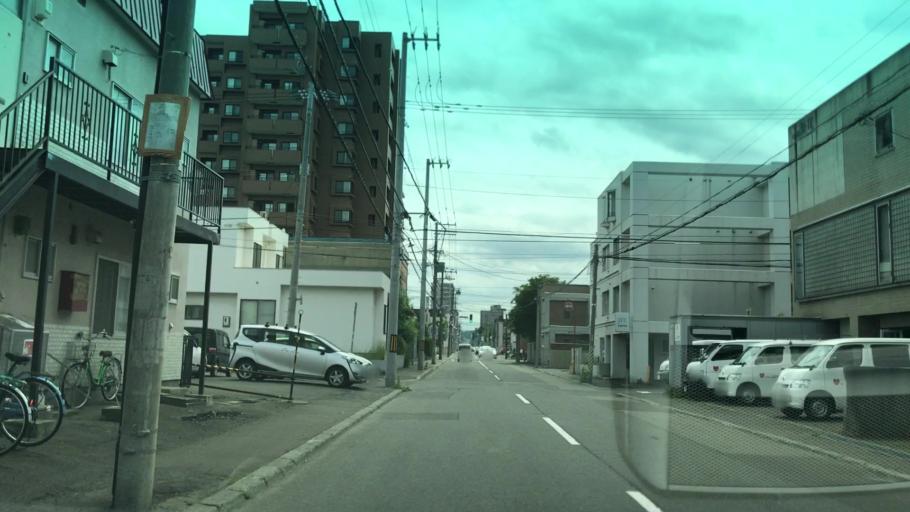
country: JP
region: Hokkaido
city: Sapporo
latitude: 43.0460
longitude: 141.3415
